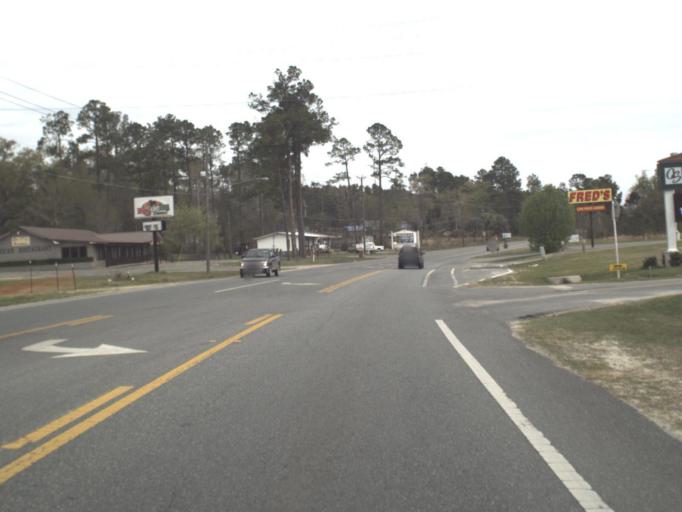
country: US
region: Florida
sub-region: Holmes County
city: Bonifay
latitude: 30.7729
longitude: -85.6842
